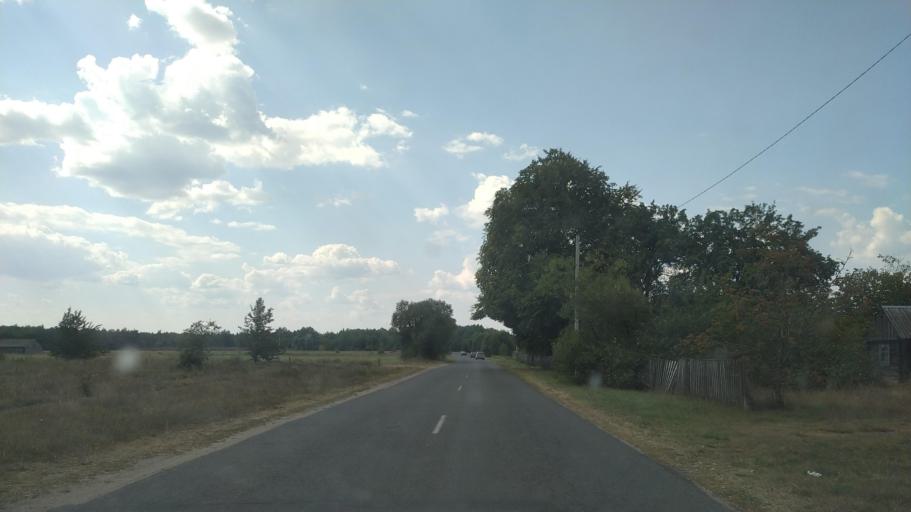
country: BY
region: Brest
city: Drahichyn
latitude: 52.1032
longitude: 25.1319
